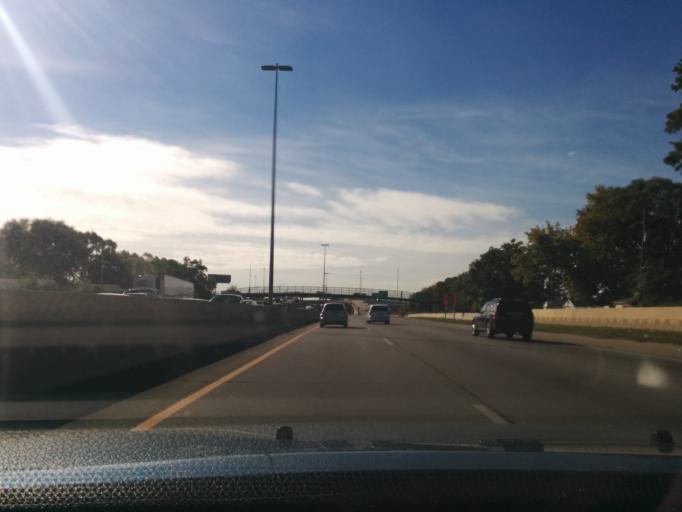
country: US
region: Michigan
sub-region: Wayne County
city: Dearborn Heights
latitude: 42.3844
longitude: -83.2176
